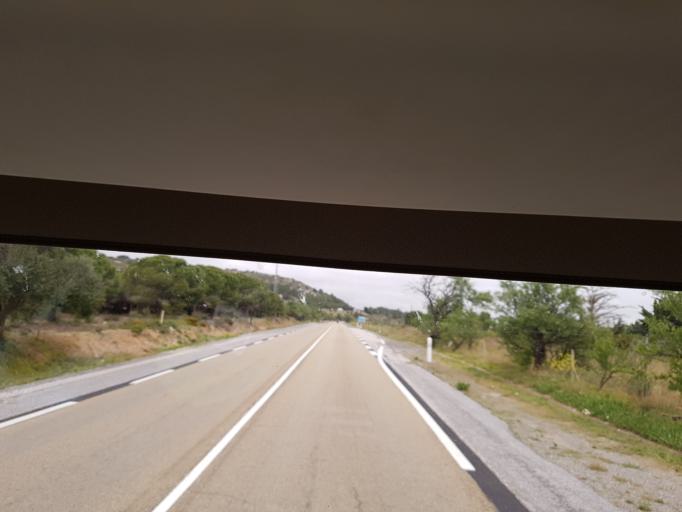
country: FR
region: Languedoc-Roussillon
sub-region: Departement de l'Aude
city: Leucate
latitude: 42.8785
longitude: 2.9933
